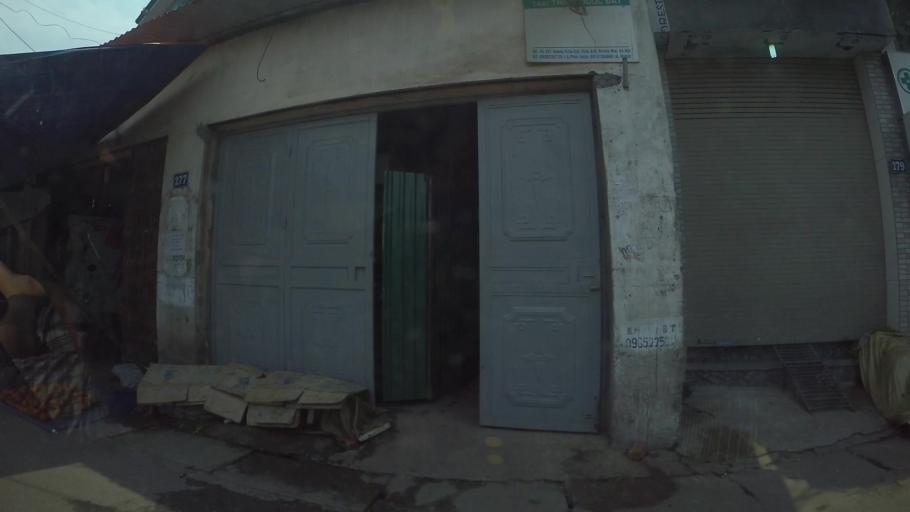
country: VN
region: Ha Noi
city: Van Dien
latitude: 20.9528
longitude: 105.8325
